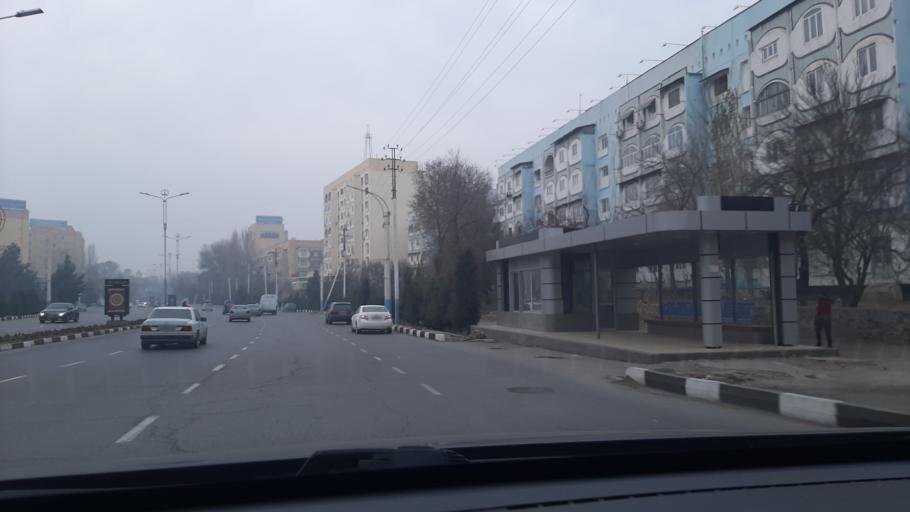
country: TJ
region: Viloyati Sughd
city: Khujand
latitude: 40.2661
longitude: 69.6535
